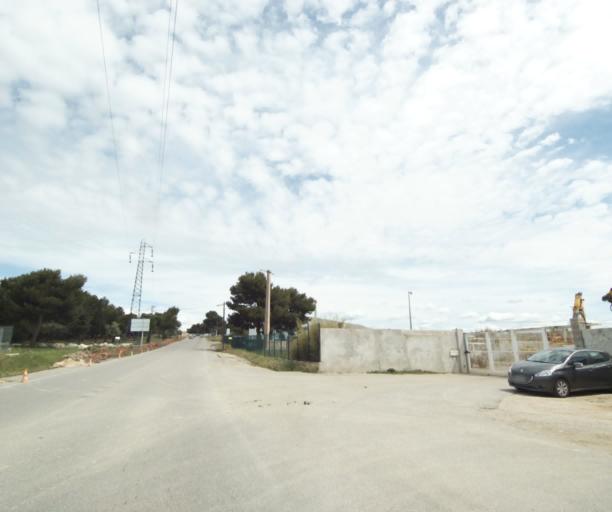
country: FR
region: Provence-Alpes-Cote d'Azur
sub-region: Departement des Bouches-du-Rhone
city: Rognac
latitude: 43.4933
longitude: 5.2047
